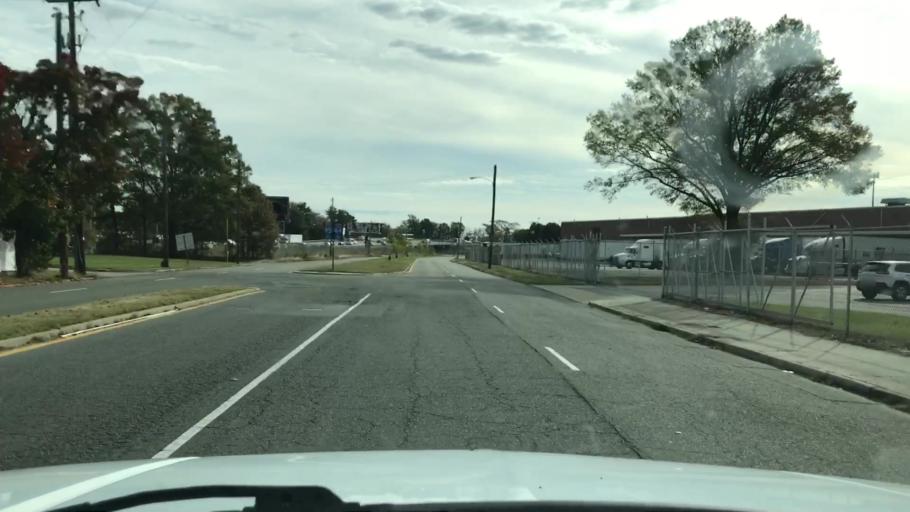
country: US
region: Virginia
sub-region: City of Richmond
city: Richmond
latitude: 37.5731
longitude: -77.4604
